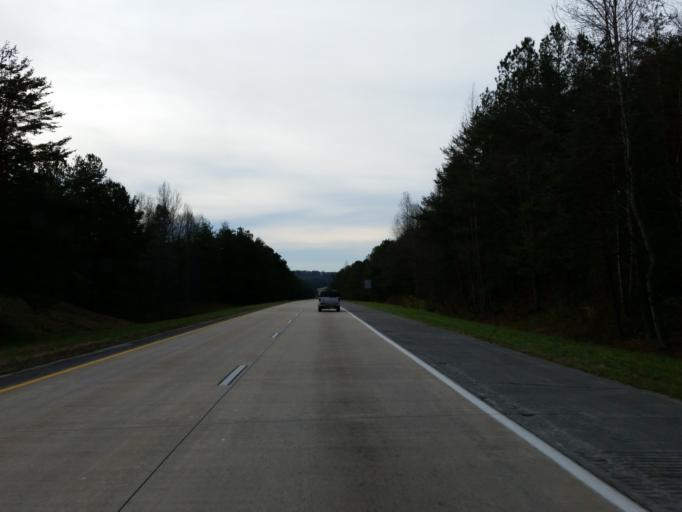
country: US
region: Georgia
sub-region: Cherokee County
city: Ball Ground
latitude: 34.3587
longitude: -84.3917
